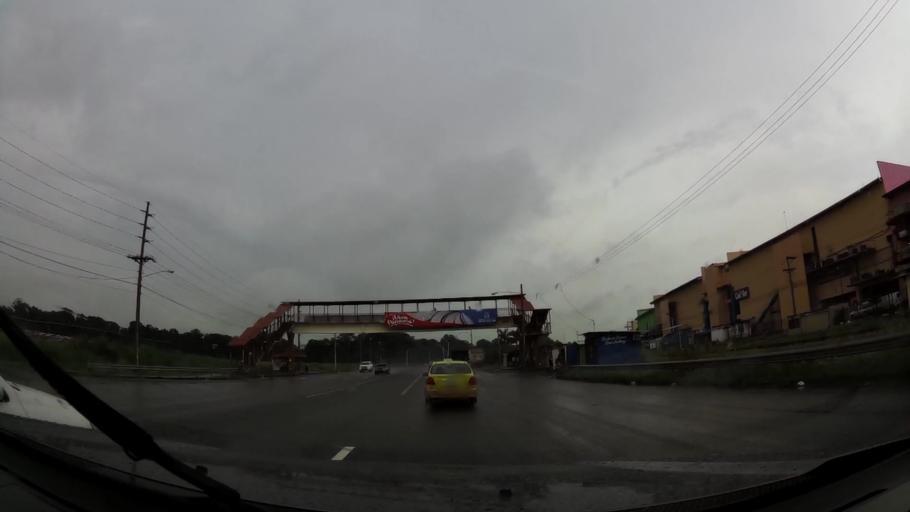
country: PA
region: Colon
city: Arco Iris
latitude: 9.3373
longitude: -79.8834
